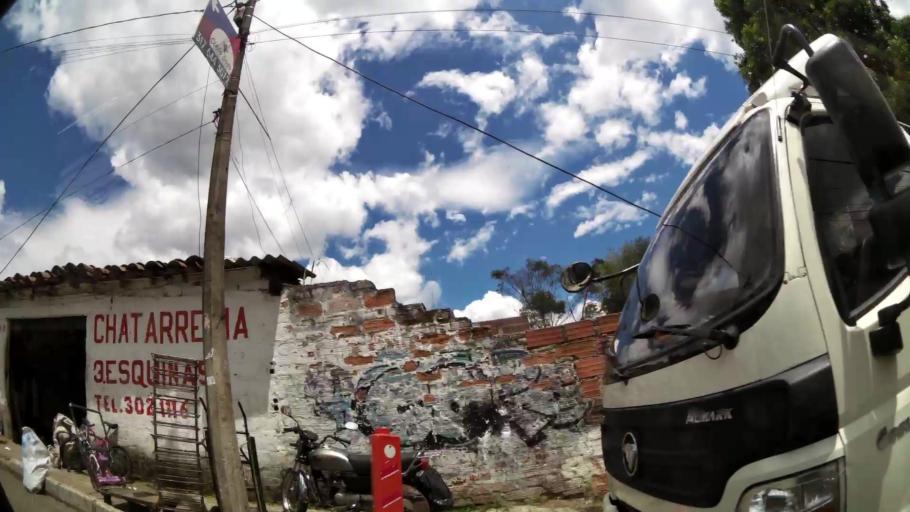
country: CO
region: Antioquia
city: La Estrella
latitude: 6.1594
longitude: -75.6415
